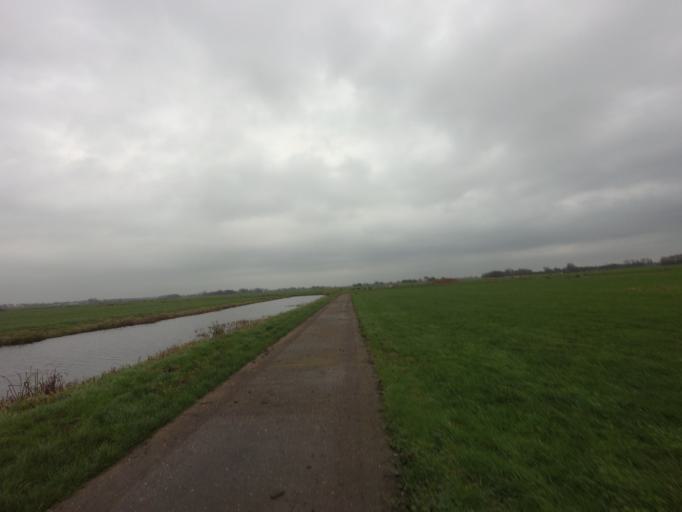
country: NL
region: Utrecht
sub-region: Gemeente De Ronde Venen
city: Mijdrecht
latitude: 52.1470
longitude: 4.8727
